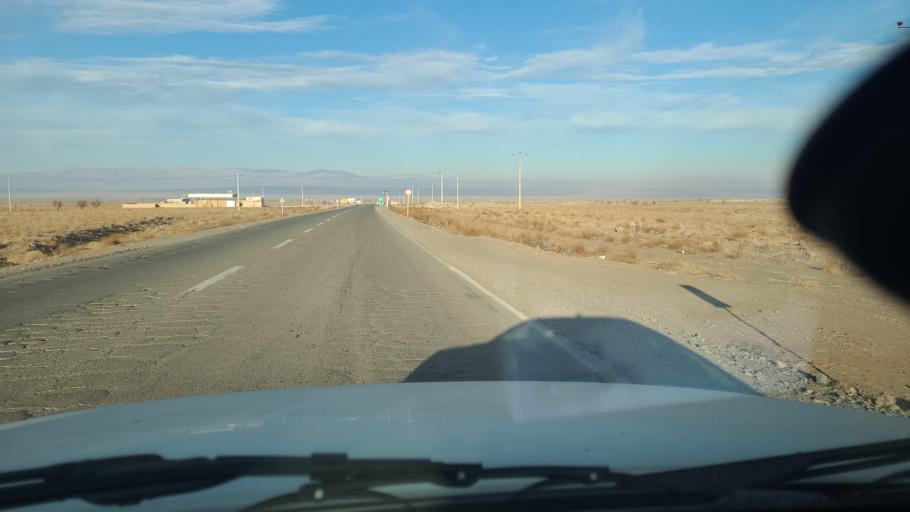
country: IR
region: Razavi Khorasan
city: Neqab
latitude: 36.5048
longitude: 57.5341
